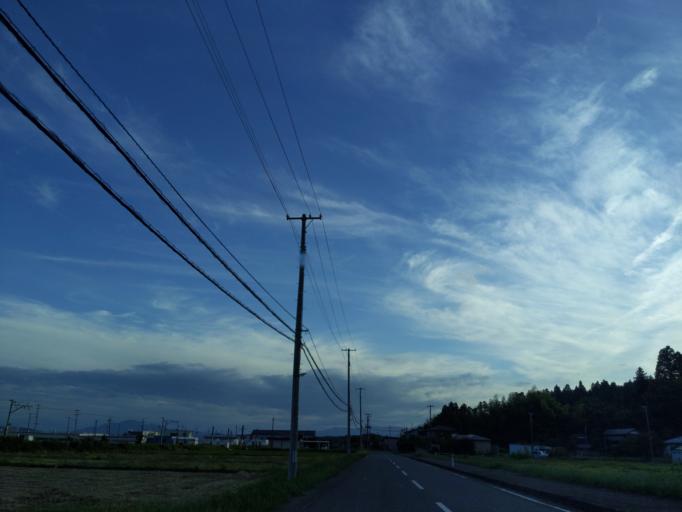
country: JP
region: Niigata
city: Kashiwazaki
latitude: 37.4379
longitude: 138.6264
